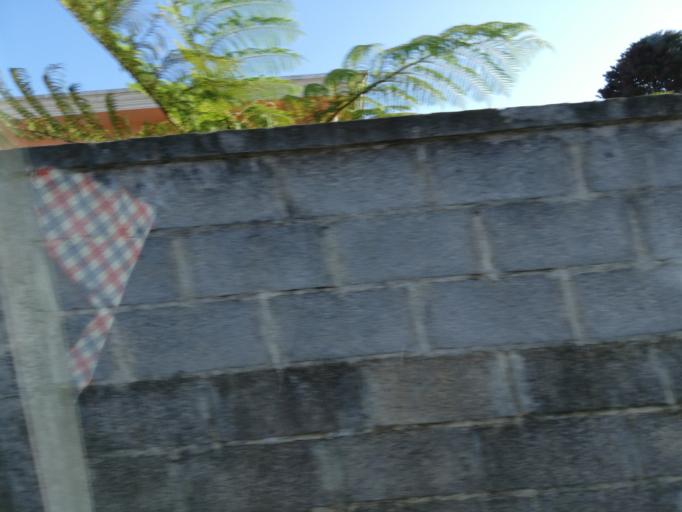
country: MU
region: Moka
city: Saint Pierre
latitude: -20.2199
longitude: 57.5246
